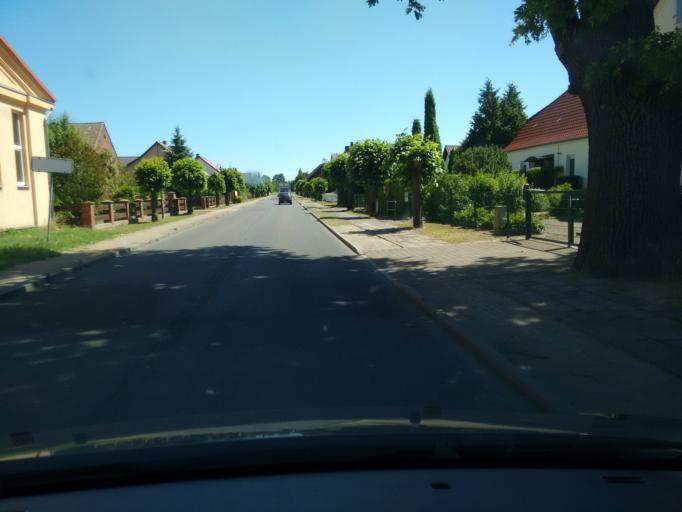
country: DE
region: Brandenburg
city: Rietz Neuendorf
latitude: 52.2125
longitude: 14.2097
